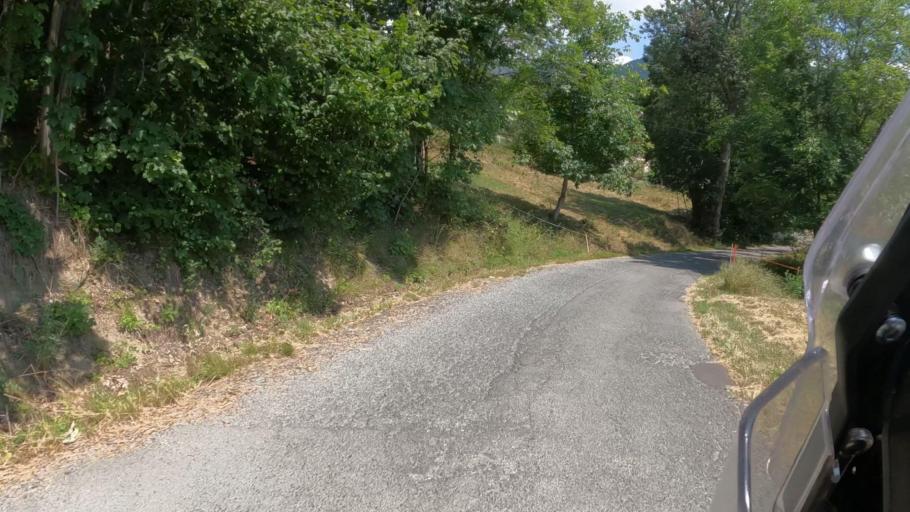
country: IT
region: Piedmont
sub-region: Provincia di Torino
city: Sant'Antonino di Susa
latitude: 45.1419
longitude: 7.2807
